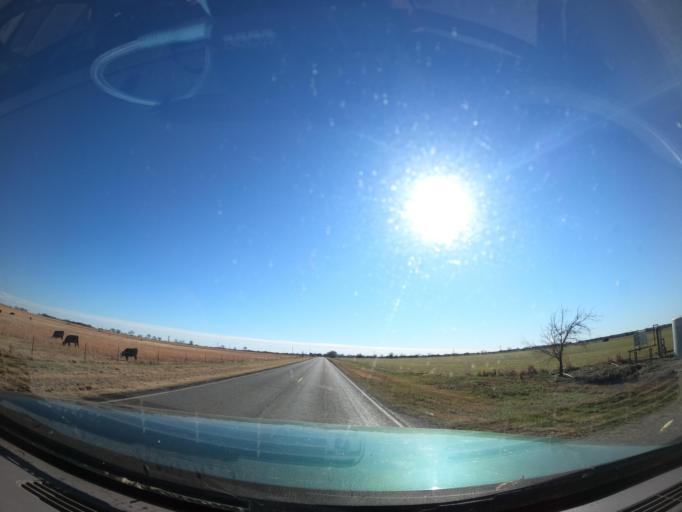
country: US
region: Oklahoma
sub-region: McIntosh County
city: Checotah
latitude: 35.5863
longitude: -95.6599
